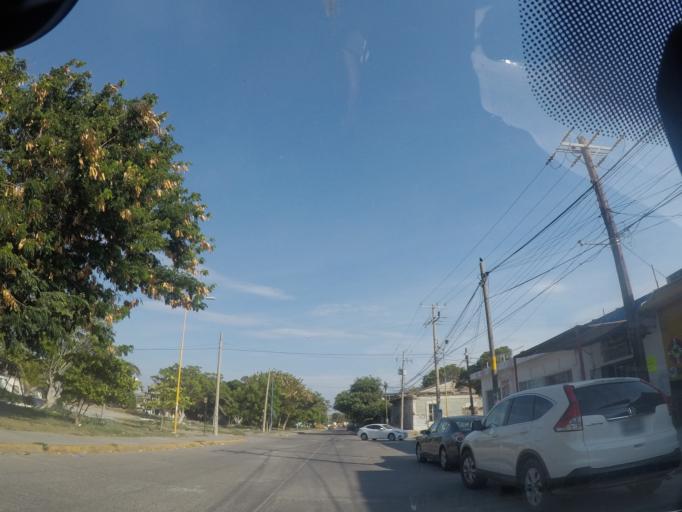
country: MX
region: Oaxaca
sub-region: Salina Cruz
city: Salina Cruz
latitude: 16.1801
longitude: -95.1988
